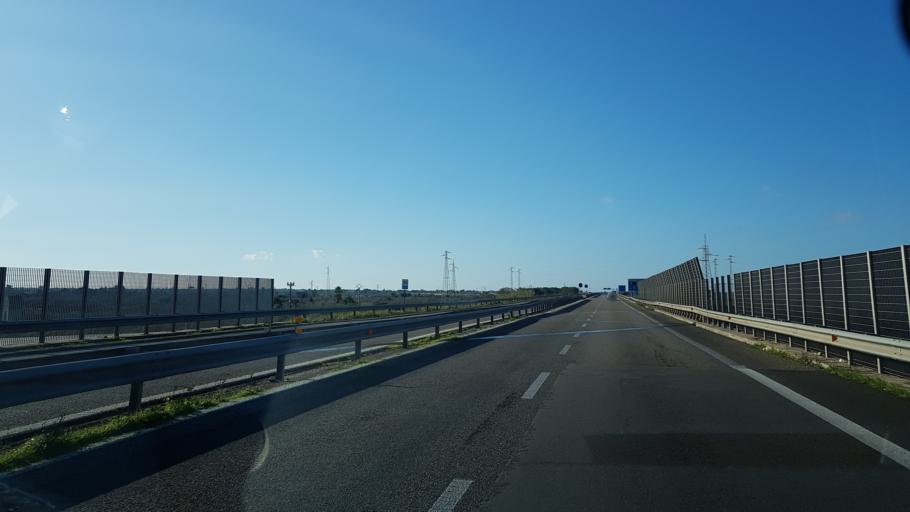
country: IT
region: Apulia
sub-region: Provincia di Lecce
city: Galatone
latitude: 40.1649
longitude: 18.0633
